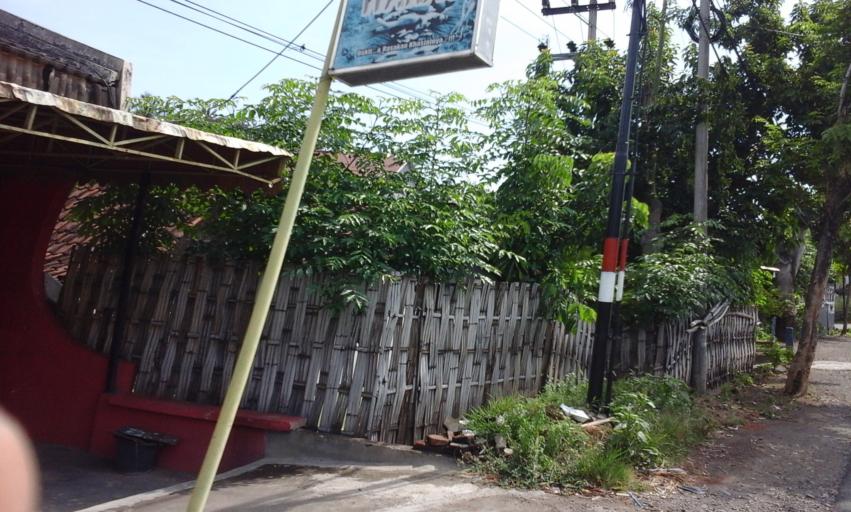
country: ID
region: East Java
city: Kepuh Wetan
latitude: -8.2542
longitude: 114.3413
